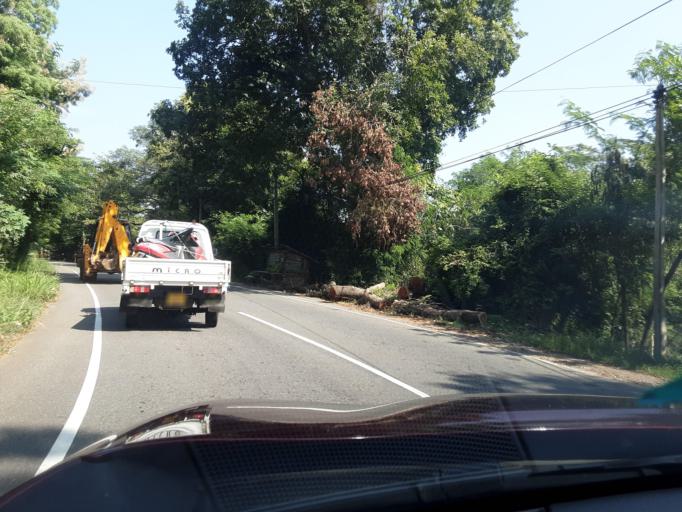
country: LK
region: Uva
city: Badulla
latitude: 7.1498
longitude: 81.0582
